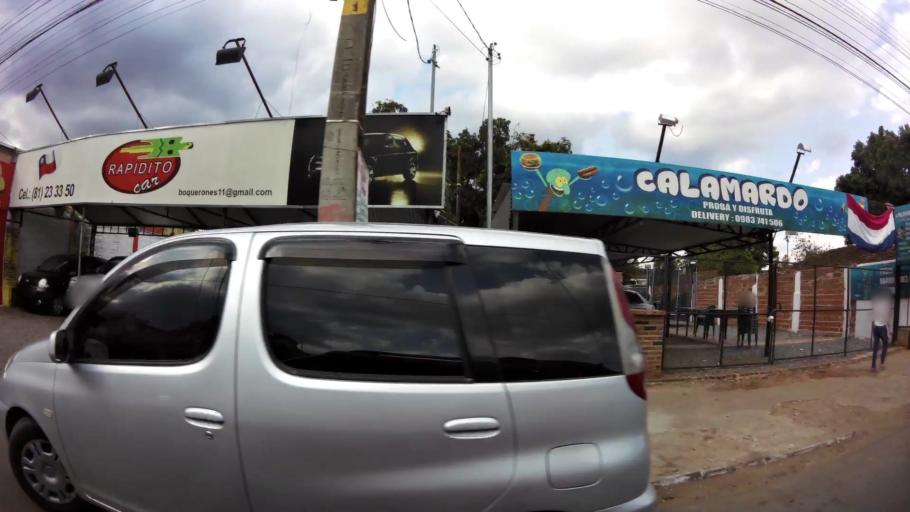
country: PY
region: Central
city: Fernando de la Mora
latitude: -25.3394
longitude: -57.5564
